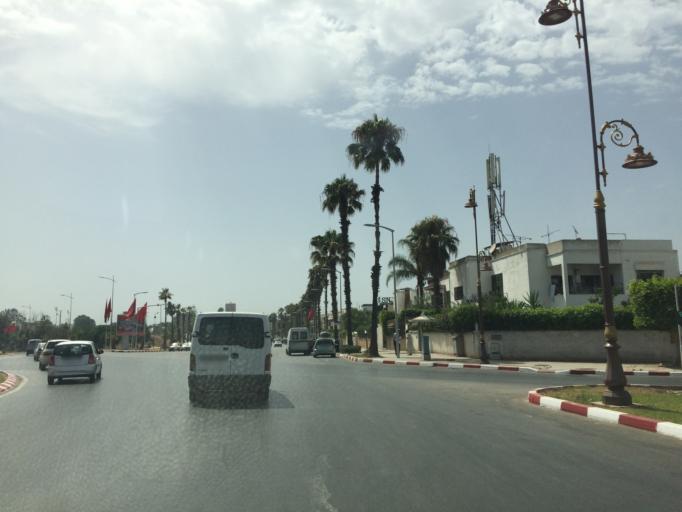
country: MA
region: Rabat-Sale-Zemmour-Zaer
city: Sale
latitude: 34.0348
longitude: -6.7876
